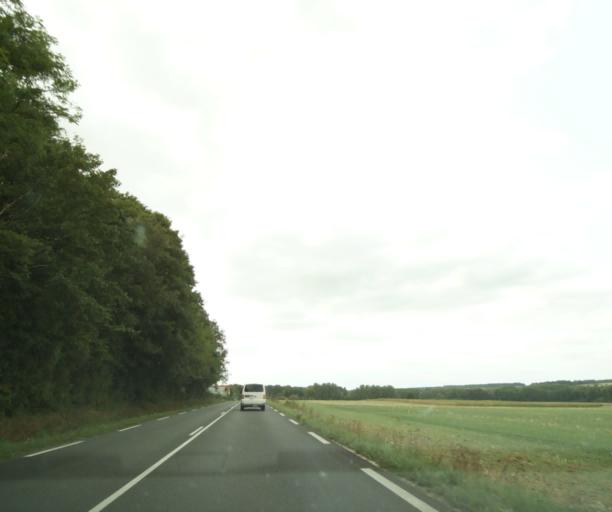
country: FR
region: Centre
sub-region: Departement d'Indre-et-Loire
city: Chambourg-sur-Indre
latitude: 47.1680
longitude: 0.9815
